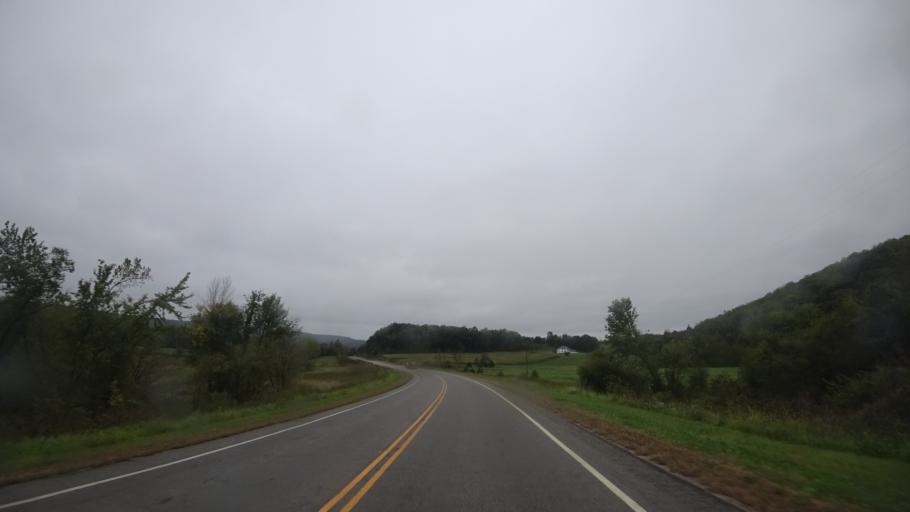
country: US
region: Wisconsin
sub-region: Crawford County
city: Prairie du Chien
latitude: 43.0455
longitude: -90.9868
